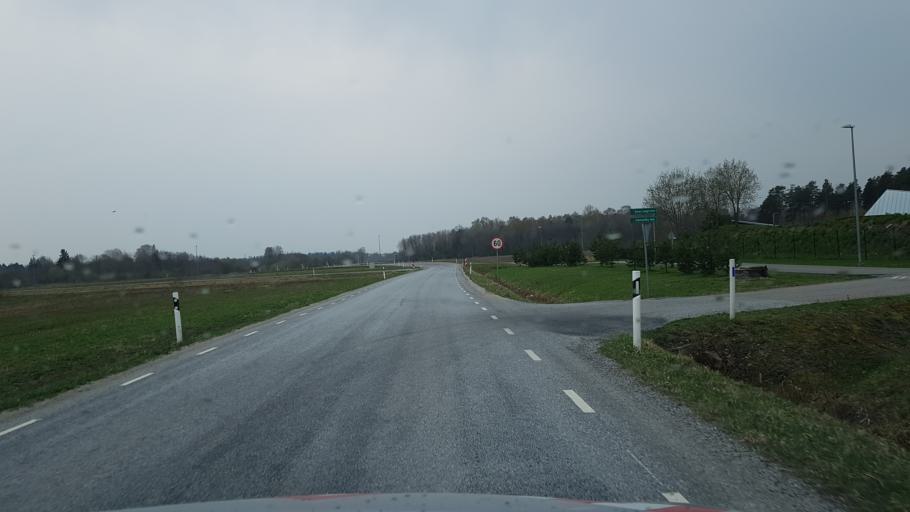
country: EE
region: Harju
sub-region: Saue vald
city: Laagri
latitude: 59.3418
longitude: 24.5896
